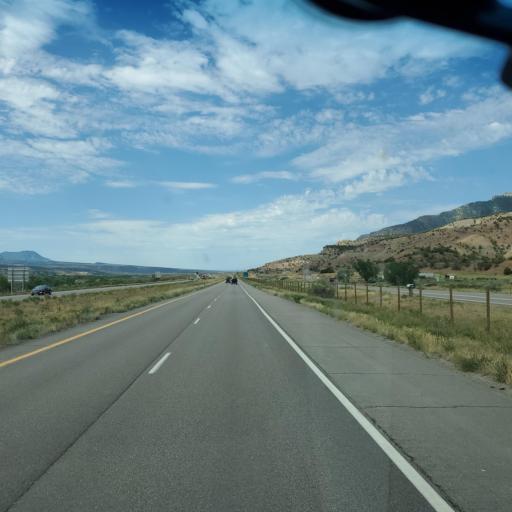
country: US
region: Colorado
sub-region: Garfield County
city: Parachute
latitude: 39.4443
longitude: -108.0599
